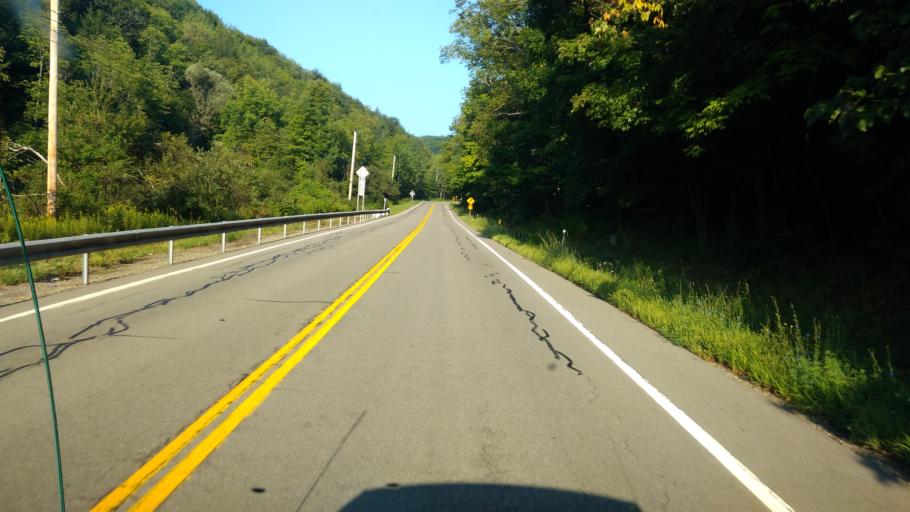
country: US
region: New York
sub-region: Allegany County
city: Andover
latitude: 42.1423
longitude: -77.6739
